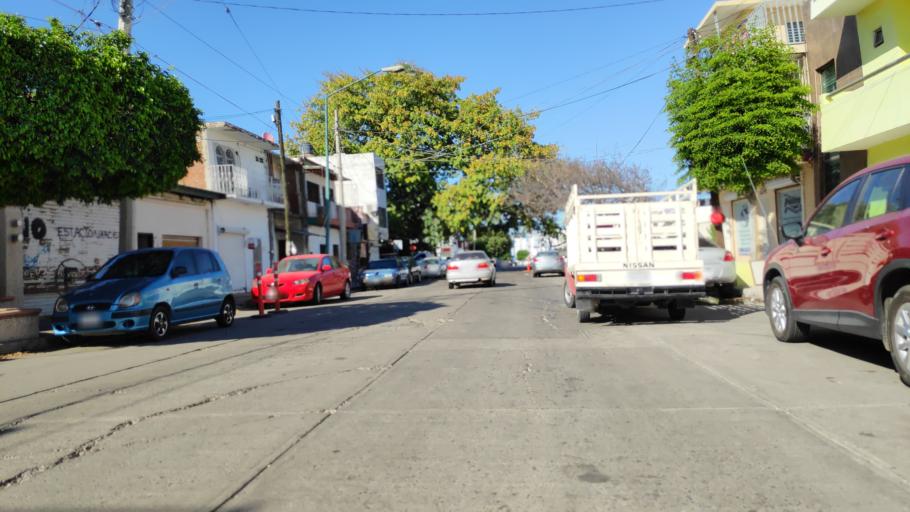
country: MX
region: Sinaloa
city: Culiacan
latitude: 24.7993
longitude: -107.3965
